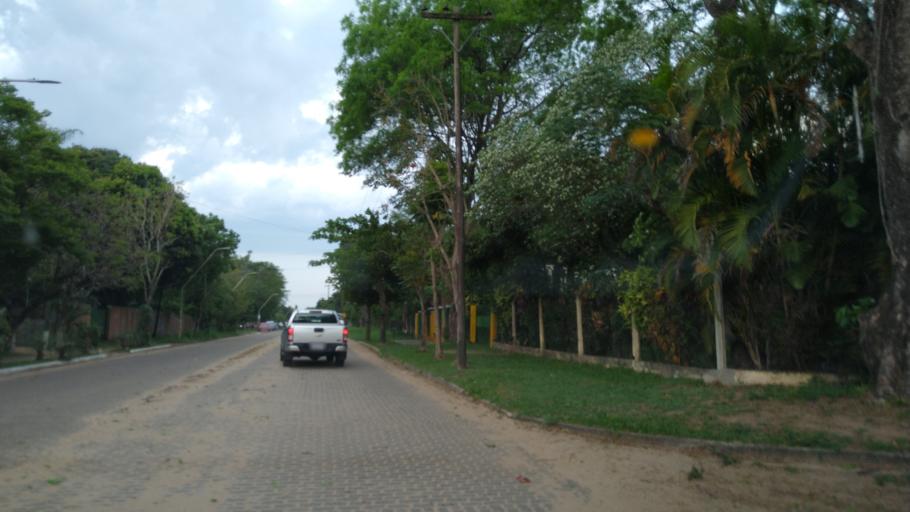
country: AR
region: Corrientes
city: Ituzaingo
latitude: -27.5906
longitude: -56.6997
